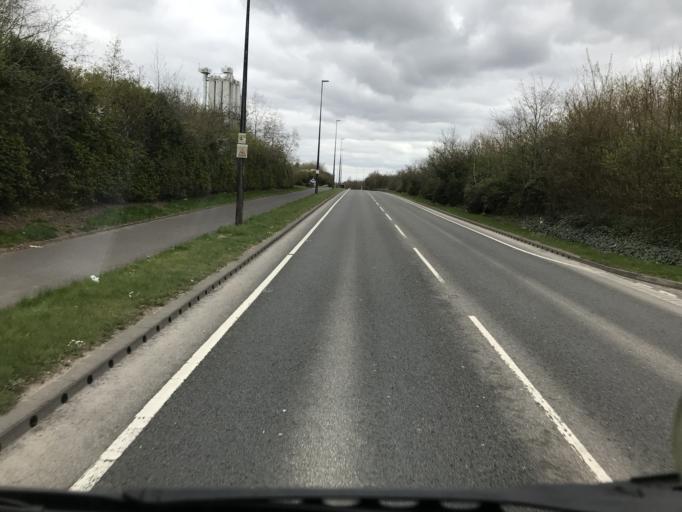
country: GB
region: England
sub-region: Trafford
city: Partington
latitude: 53.4254
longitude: -2.4289
